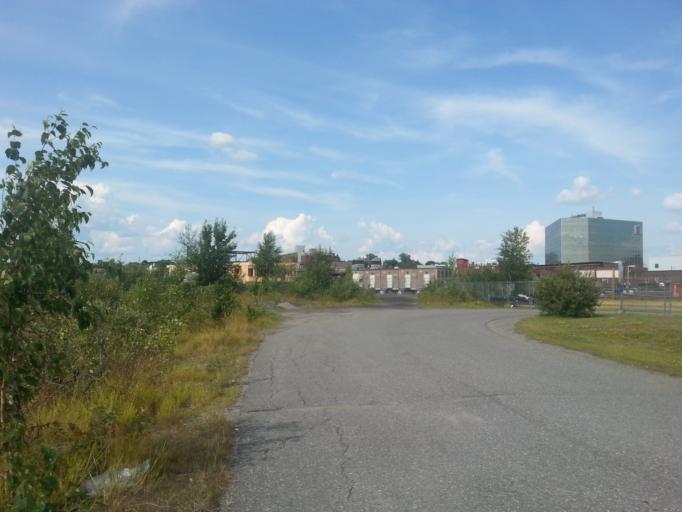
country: CA
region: Ontario
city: Greater Sudbury
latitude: 46.4908
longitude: -80.9980
